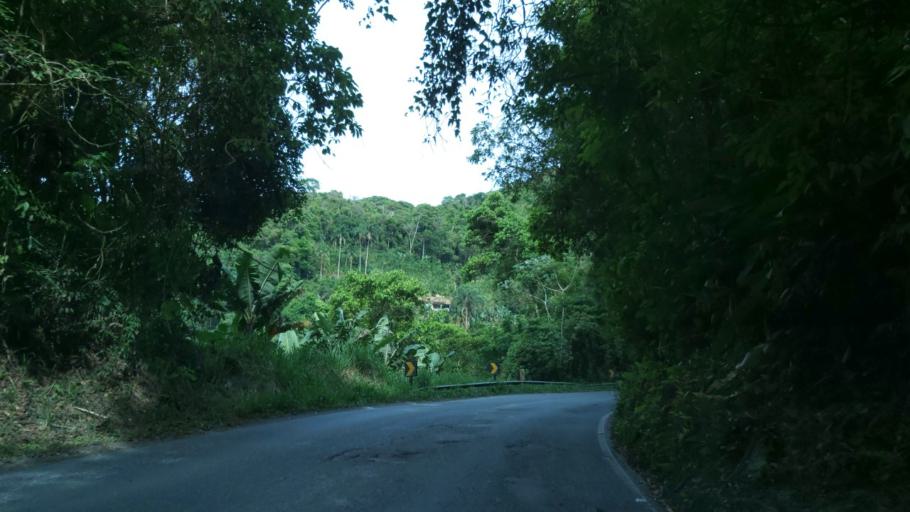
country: BR
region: Sao Paulo
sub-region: Juquia
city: Juquia
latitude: -24.1113
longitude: -47.6288
